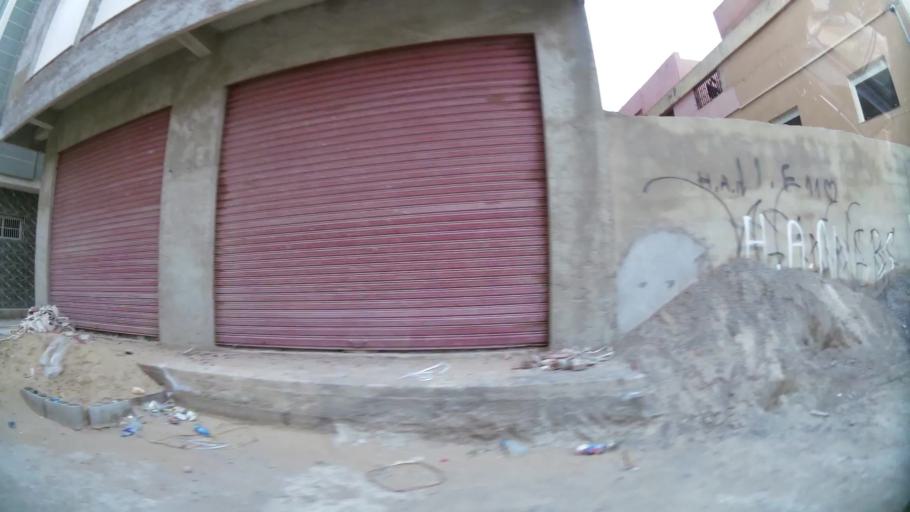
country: MA
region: Oriental
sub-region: Nador
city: Nador
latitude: 35.1700
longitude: -2.9353
